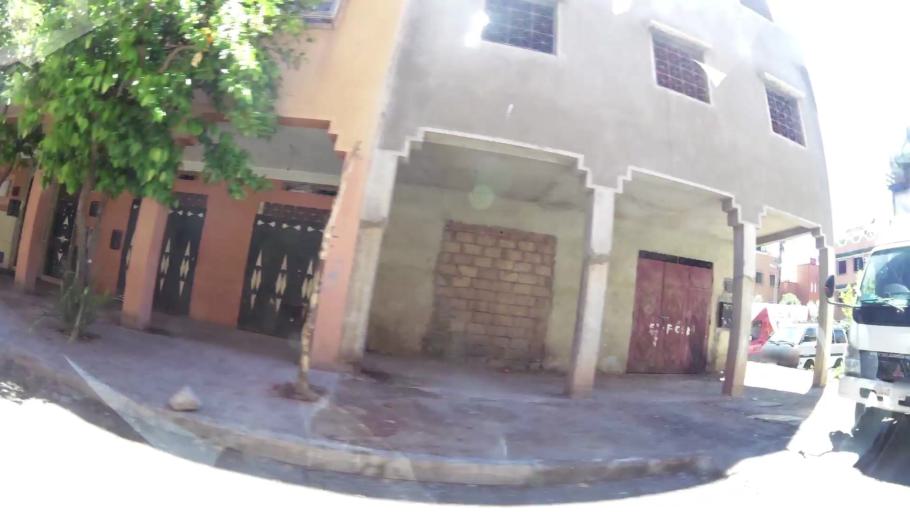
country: MA
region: Marrakech-Tensift-Al Haouz
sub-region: Marrakech
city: Marrakesh
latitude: 31.6307
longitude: -8.0608
